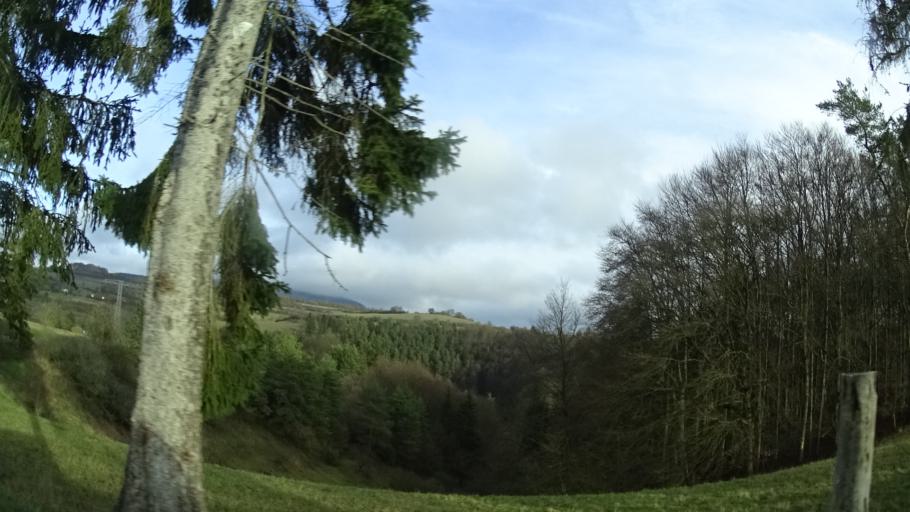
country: DE
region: Thuringia
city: Utendorf
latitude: 50.5997
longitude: 10.4381
